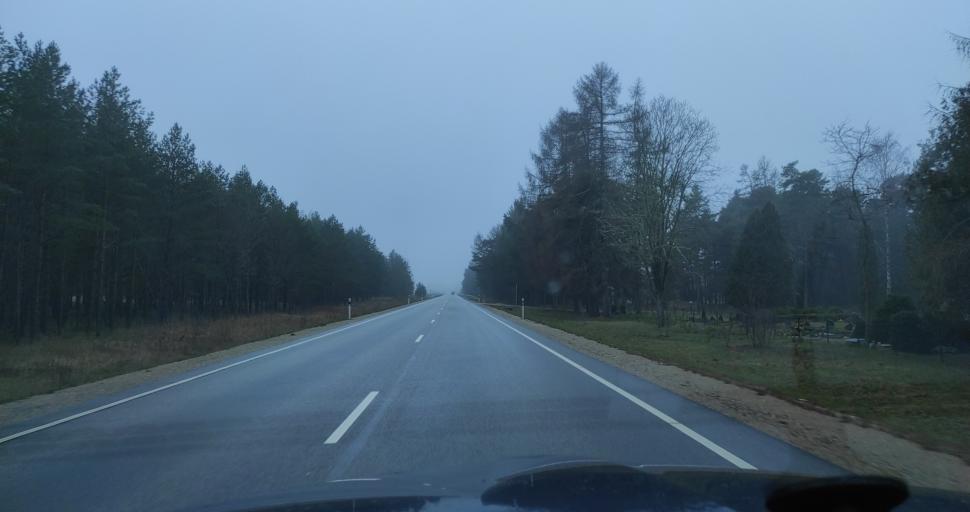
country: LV
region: Pavilostas
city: Pavilosta
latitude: 56.9431
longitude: 21.2864
